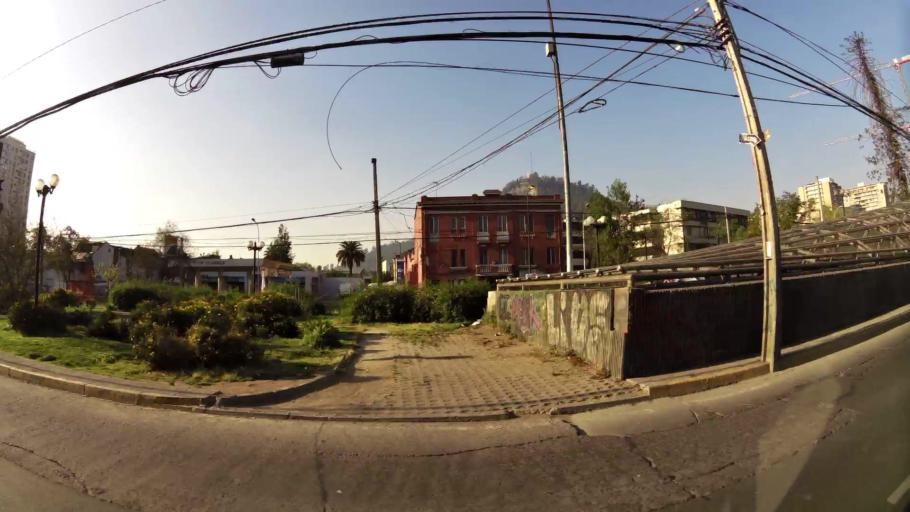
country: CL
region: Santiago Metropolitan
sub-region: Provincia de Santiago
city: Santiago
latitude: -33.4346
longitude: -70.6399
